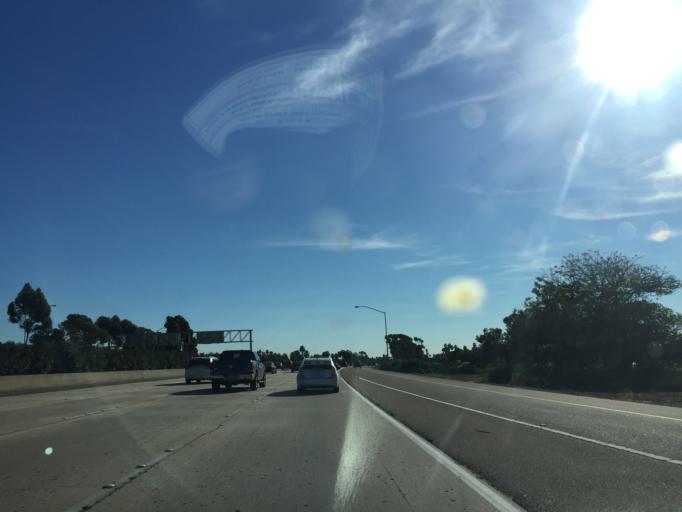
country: US
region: California
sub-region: San Diego County
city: La Jolla
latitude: 32.7893
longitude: -117.2072
